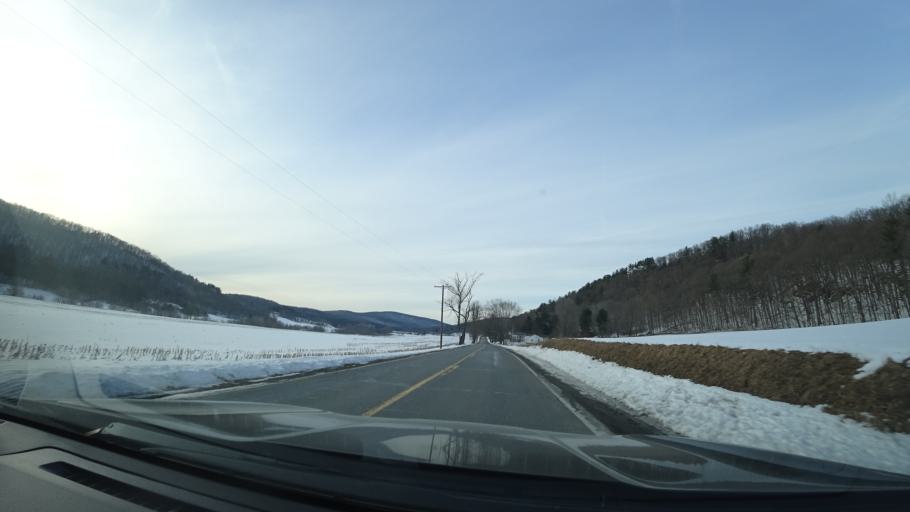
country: US
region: New York
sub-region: Washington County
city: Cambridge
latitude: 43.1786
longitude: -73.3651
